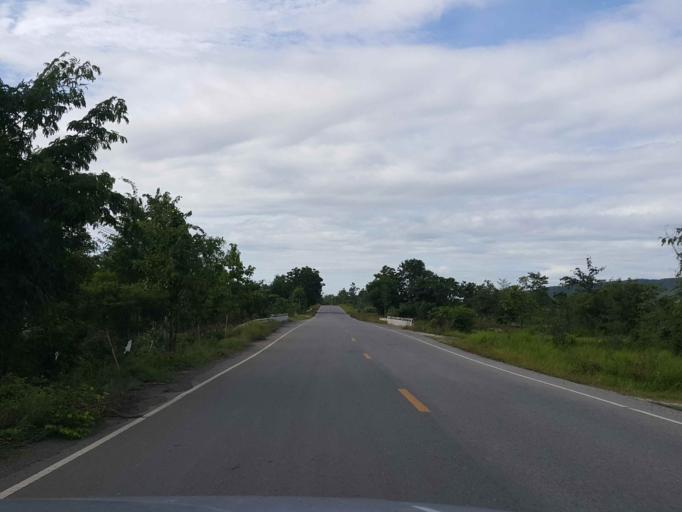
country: TH
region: Sukhothai
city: Thung Saliam
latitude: 17.2416
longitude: 99.5159
